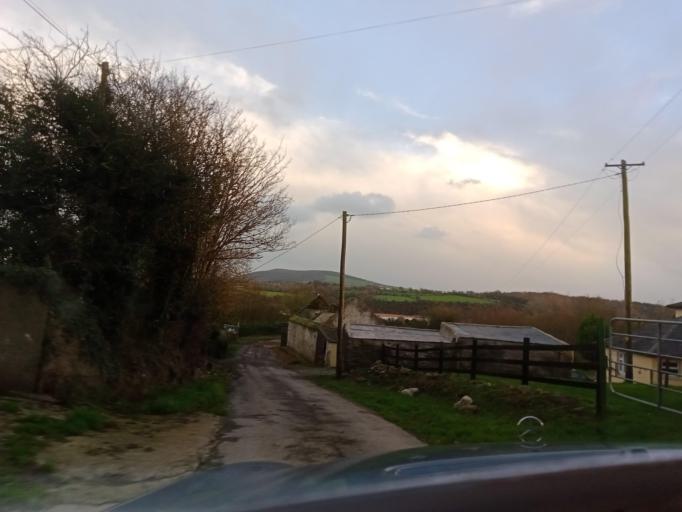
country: IE
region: Leinster
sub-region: Loch Garman
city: New Ross
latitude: 52.3451
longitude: -7.0025
